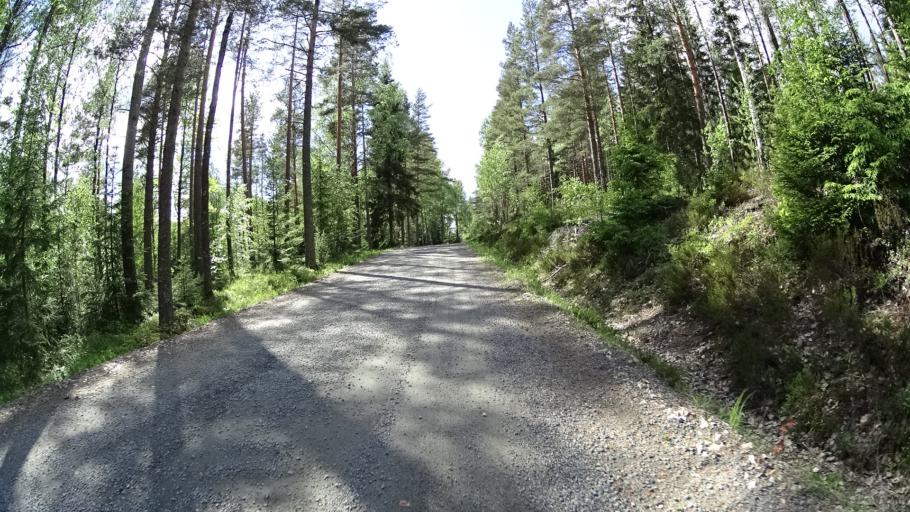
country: FI
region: Varsinais-Suomi
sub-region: Salo
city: Kisko
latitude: 60.1881
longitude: 23.5707
